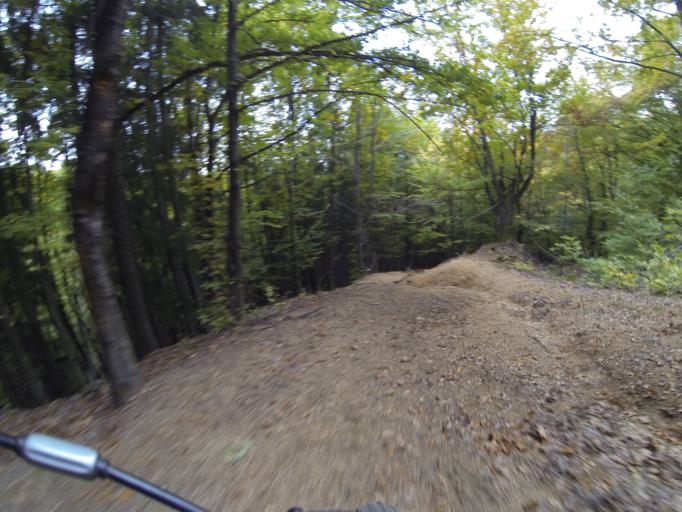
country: RO
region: Gorj
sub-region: Comuna Tismana
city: Sohodol
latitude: 45.0892
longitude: 22.8855
